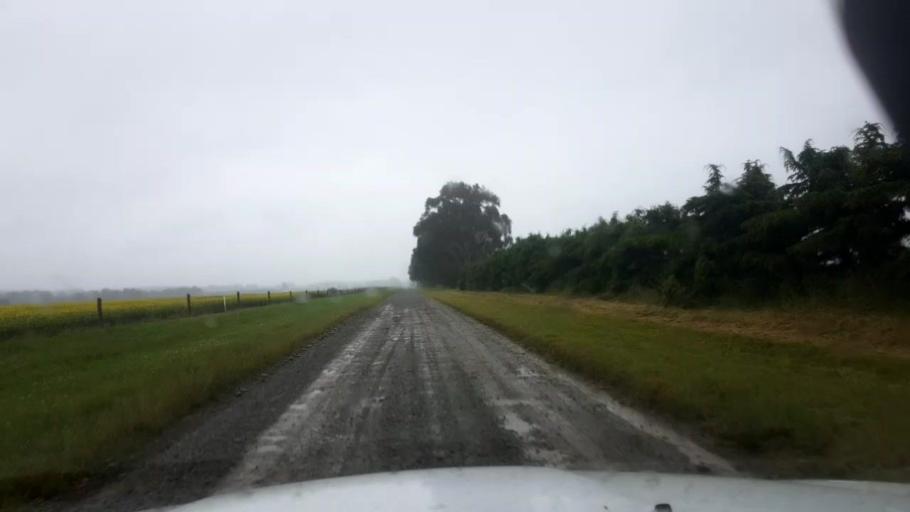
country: NZ
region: Canterbury
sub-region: Timaru District
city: Pleasant Point
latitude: -44.2882
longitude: 171.2119
